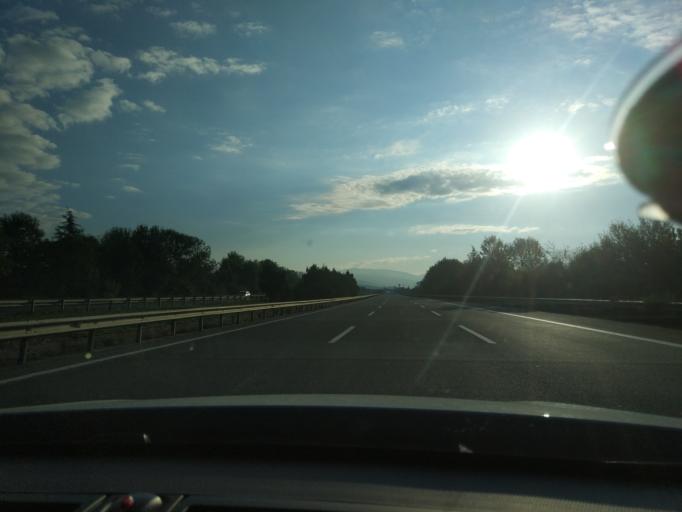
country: TR
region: Duzce
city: Duzce
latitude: 40.7911
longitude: 31.2179
